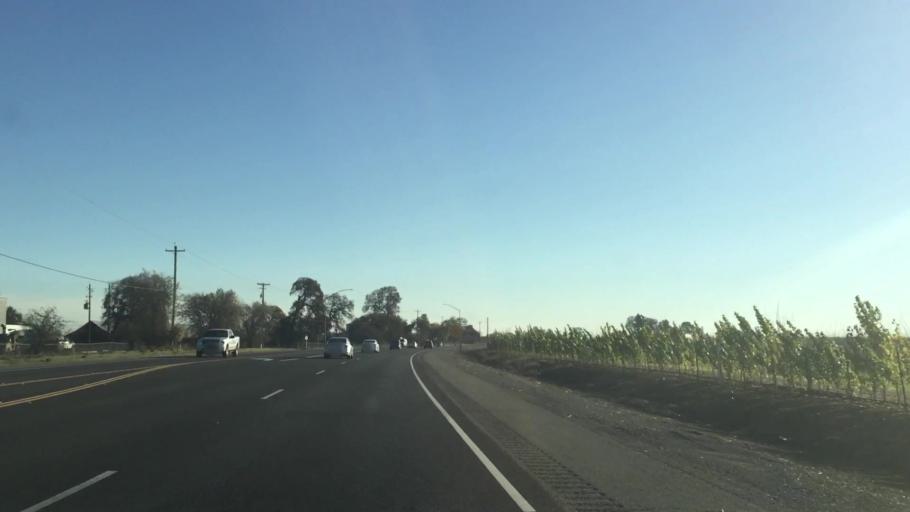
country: US
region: California
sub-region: Butte County
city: Gridley
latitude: 39.3515
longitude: -121.6020
